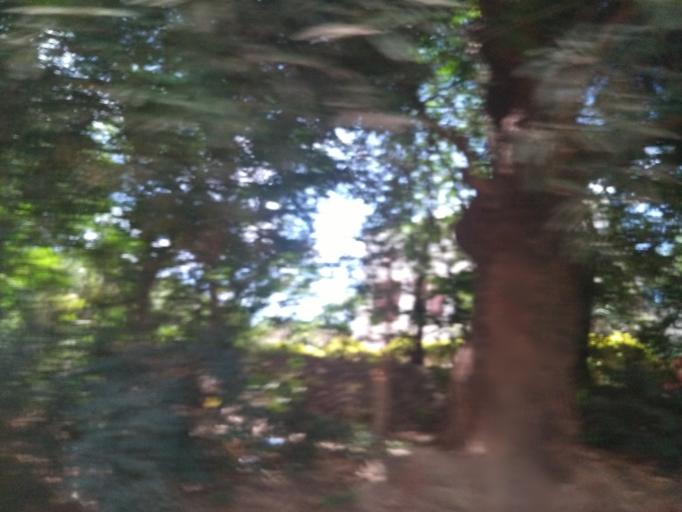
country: TZ
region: Mwanza
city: Mwanza
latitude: -2.5069
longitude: 32.9093
